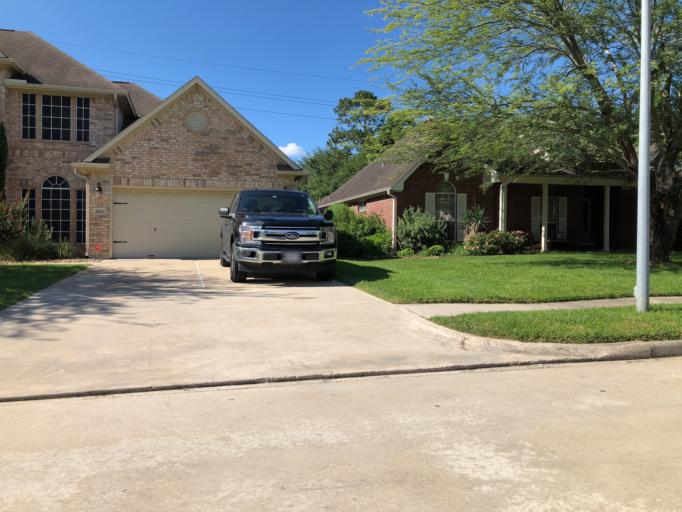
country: US
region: Texas
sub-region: Harris County
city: Katy
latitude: 29.8084
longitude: -95.8286
